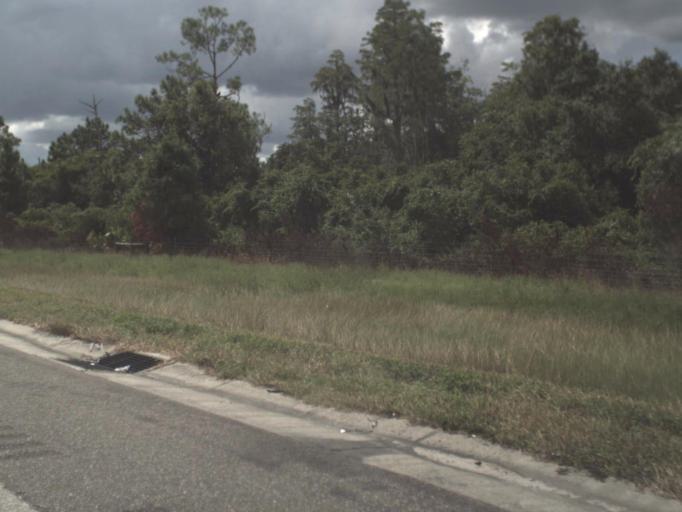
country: US
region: Florida
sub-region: Polk County
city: Lake Alfred
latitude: 28.1971
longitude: -81.7088
